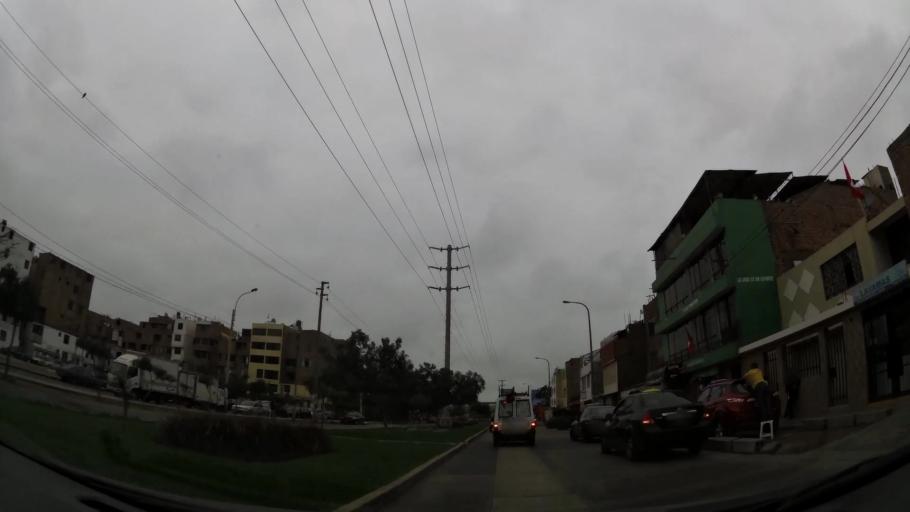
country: PE
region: Lima
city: Lima
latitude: -12.0597
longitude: -77.0634
